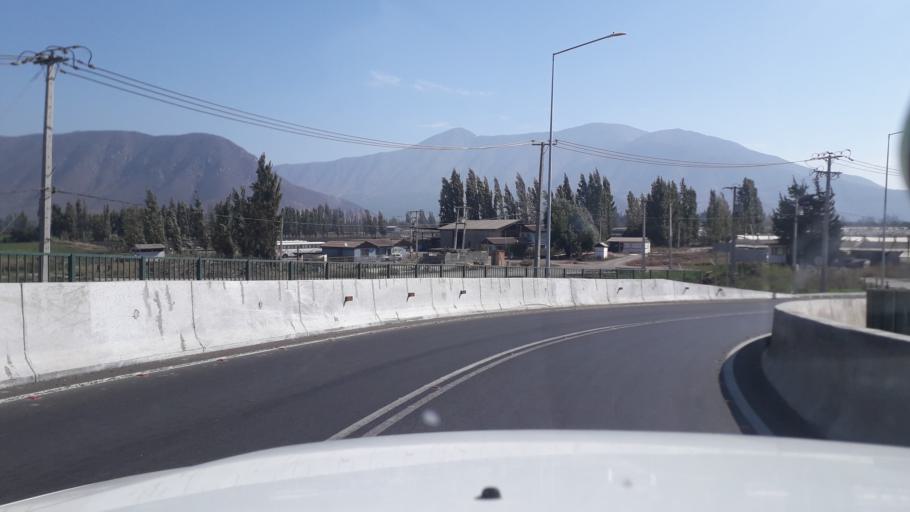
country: CL
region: Valparaiso
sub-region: Provincia de San Felipe
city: Llaillay
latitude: -32.8492
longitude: -70.9608
